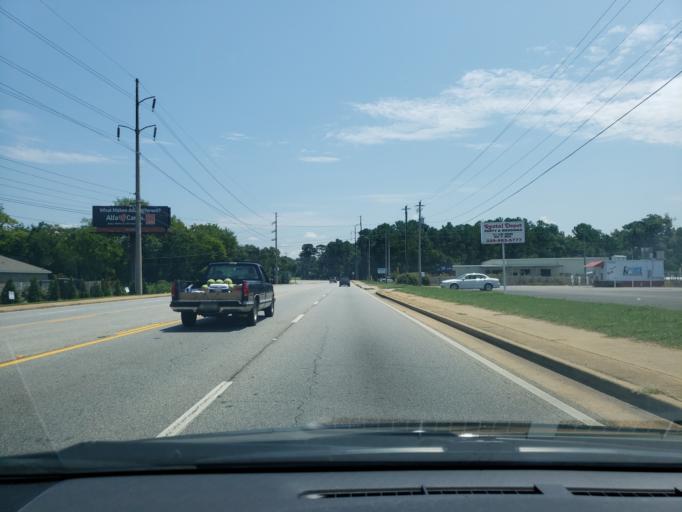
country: US
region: Georgia
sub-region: Dougherty County
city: Albany
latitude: 31.5835
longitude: -84.2036
